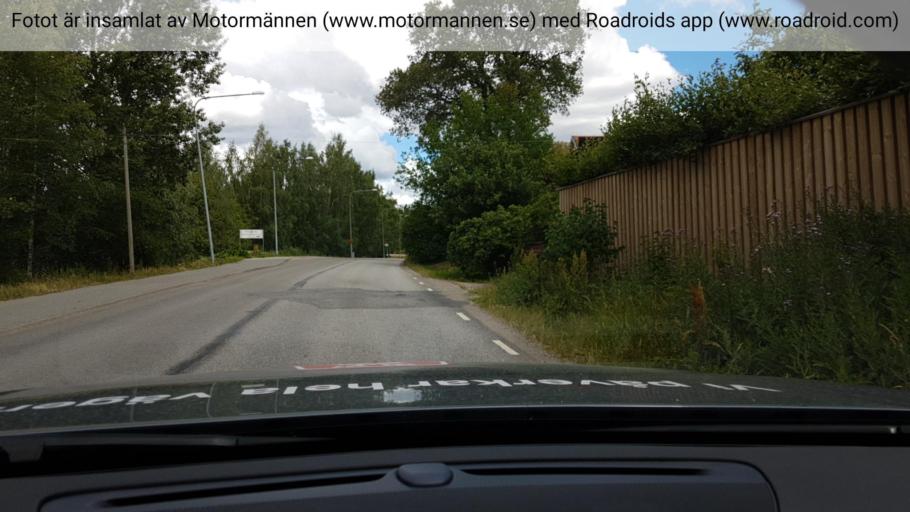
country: SE
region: Stockholm
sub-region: Huddinge Kommun
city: Huddinge
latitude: 59.2317
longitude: 17.9980
